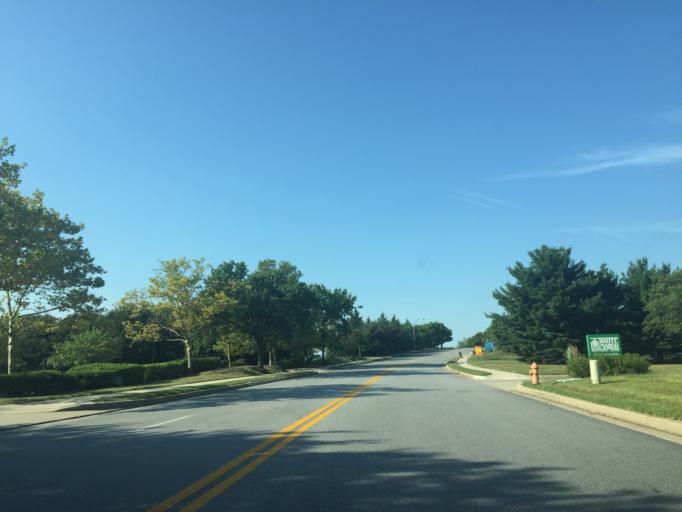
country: US
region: Maryland
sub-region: Baltimore County
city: Rossville
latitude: 39.3720
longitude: -76.4710
